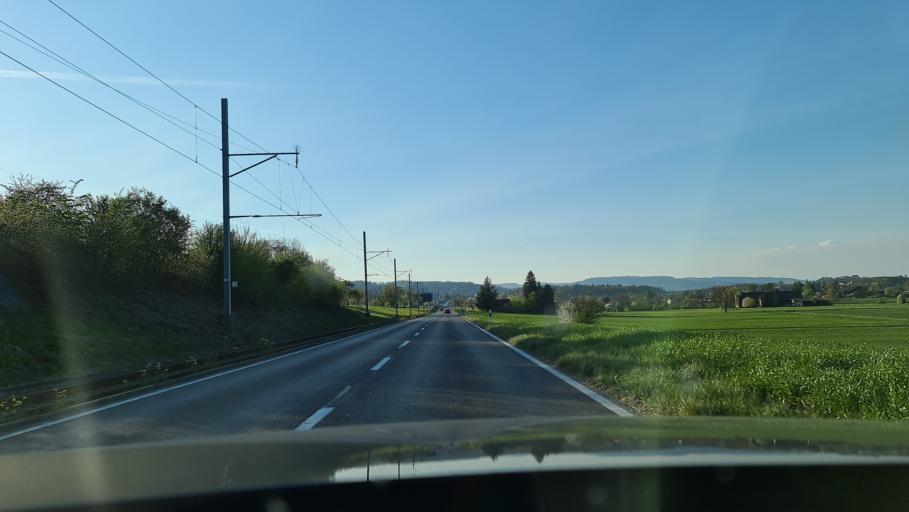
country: CH
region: Aargau
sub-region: Bezirk Lenzburg
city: Seon
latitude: 47.3349
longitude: 8.1697
